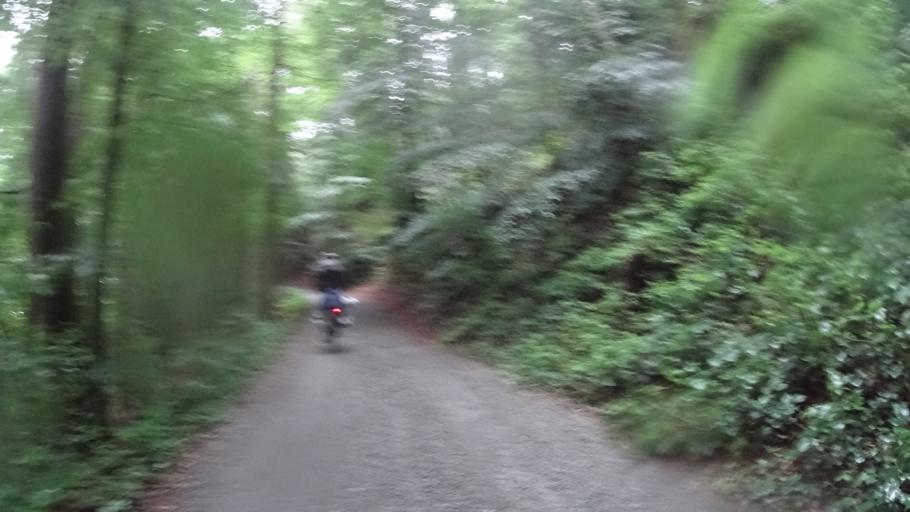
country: AT
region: Upper Austria
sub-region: Politischer Bezirk Scharding
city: Scharding
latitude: 48.4955
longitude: 13.4465
